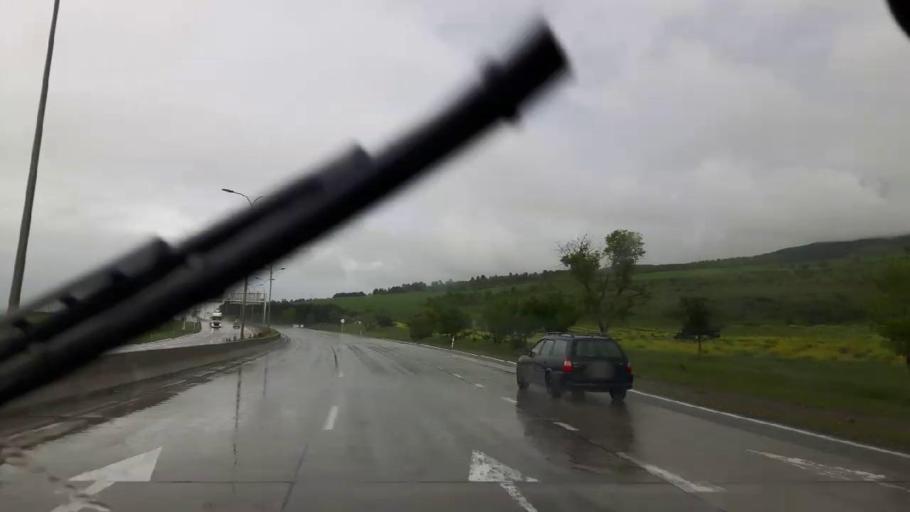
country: GE
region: Shida Kartli
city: Gori
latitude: 42.0256
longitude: 44.2101
